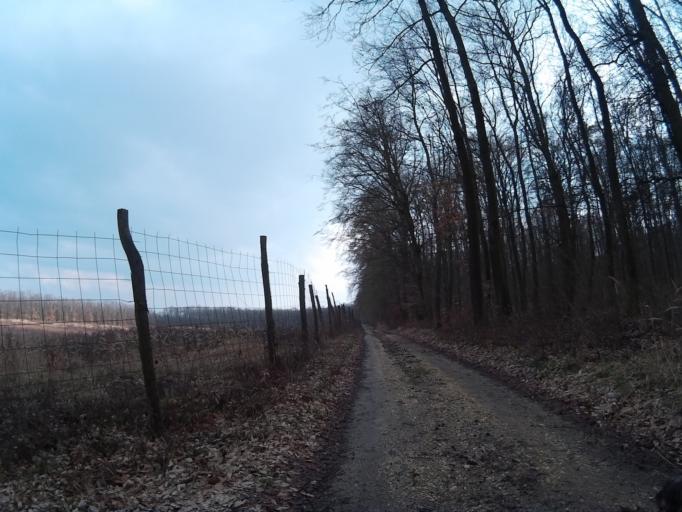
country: HU
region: Vas
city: Sarvar
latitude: 47.1362
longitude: 16.9898
